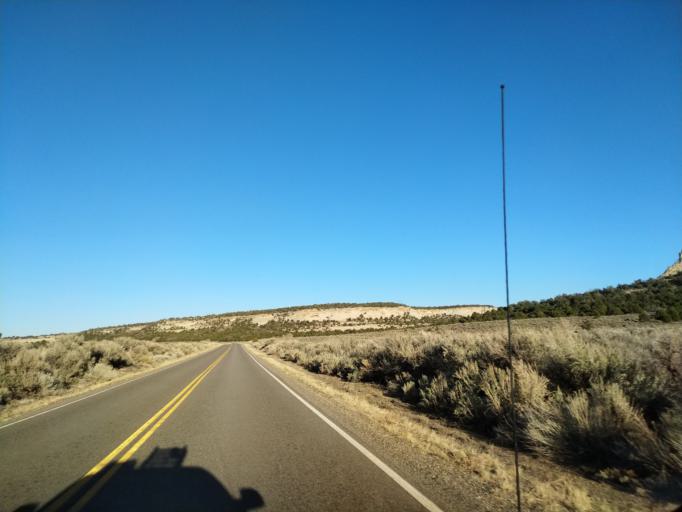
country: US
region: Colorado
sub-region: Mesa County
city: Fruita
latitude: 38.9834
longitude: -108.8053
